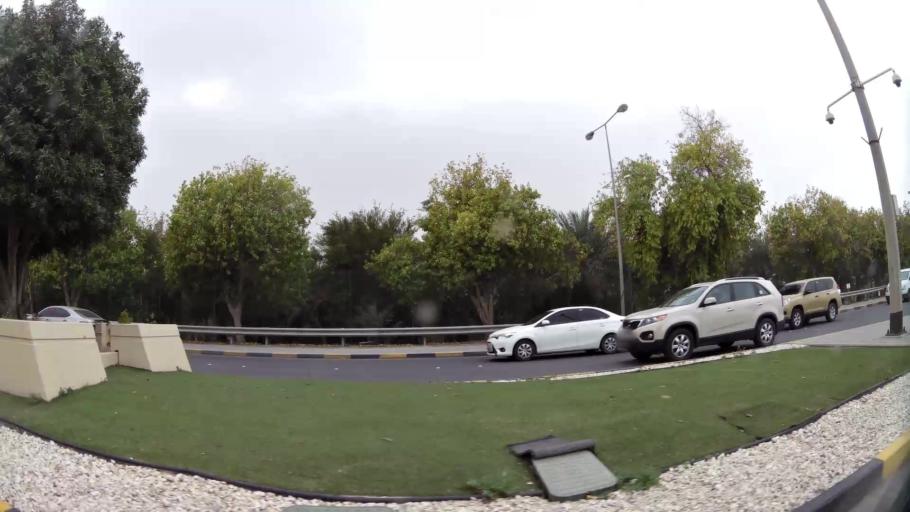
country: BH
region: Northern
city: Ar Rifa'
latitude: 26.1412
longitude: 50.5431
